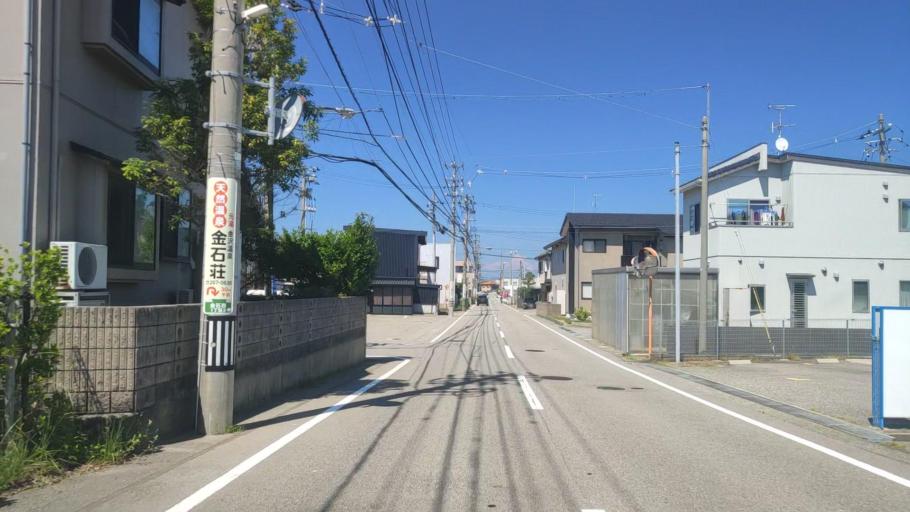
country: JP
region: Ishikawa
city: Kanazawa-shi
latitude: 36.5989
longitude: 136.5919
